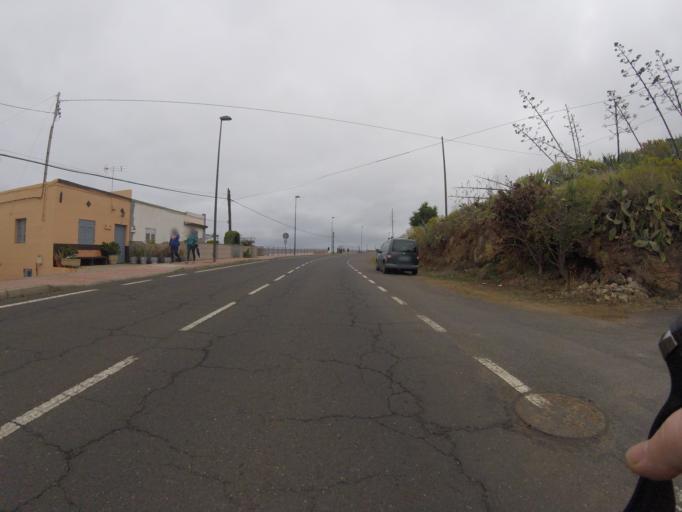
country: ES
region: Canary Islands
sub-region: Provincia de Santa Cruz de Tenerife
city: Tegueste
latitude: 28.5305
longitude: -16.3716
